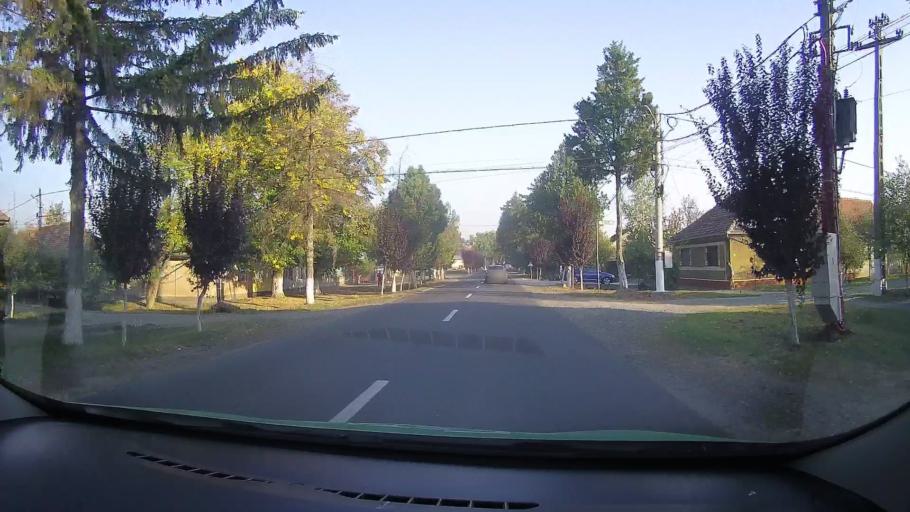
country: RO
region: Arad
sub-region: Comuna Curtici
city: Curtici
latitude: 46.3374
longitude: 21.3083
